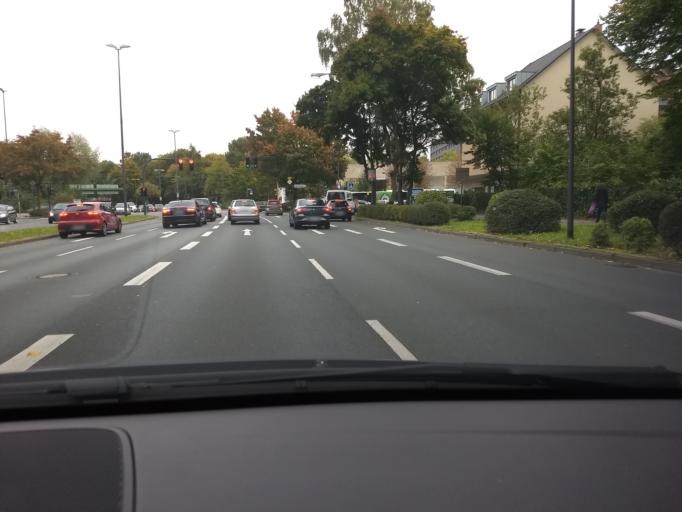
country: DE
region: North Rhine-Westphalia
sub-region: Regierungsbezirk Dusseldorf
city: Essen
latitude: 51.4647
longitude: 7.0003
